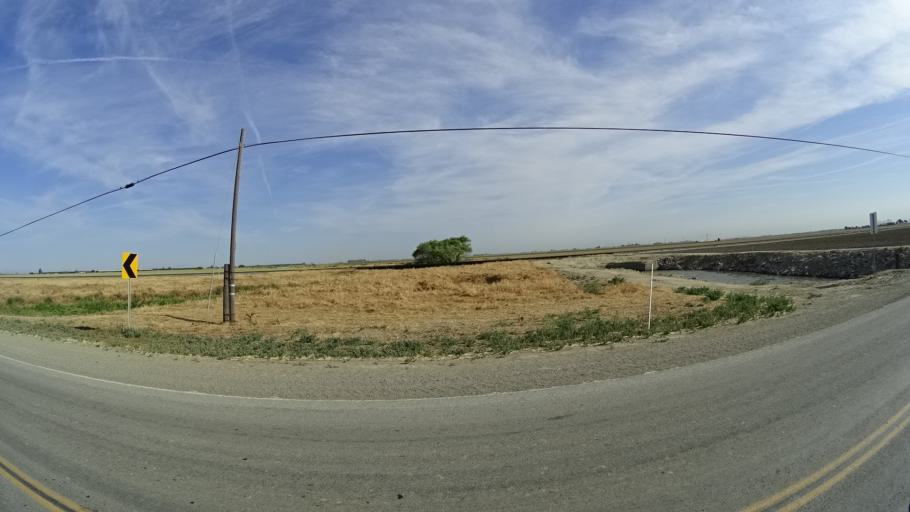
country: US
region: California
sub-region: Tulare County
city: Goshen
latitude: 36.3427
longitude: -119.5240
